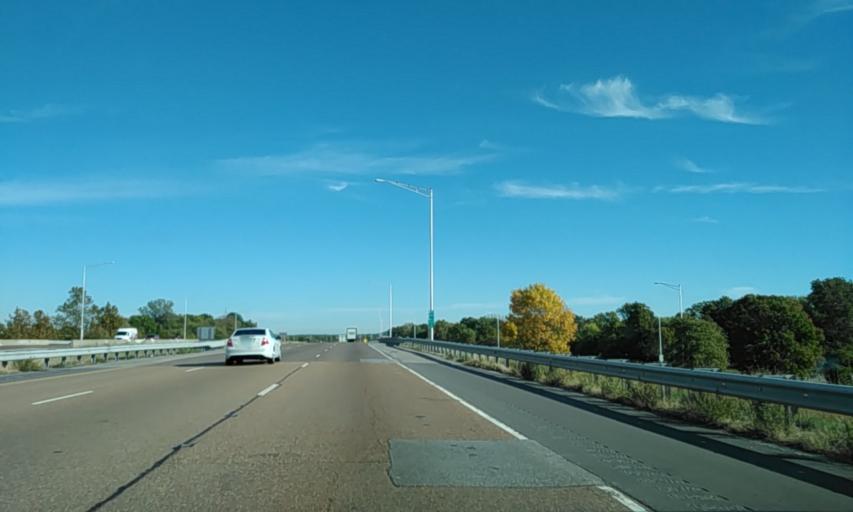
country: US
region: Illinois
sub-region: Saint Clair County
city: Caseyville
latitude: 38.6589
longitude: -90.0311
